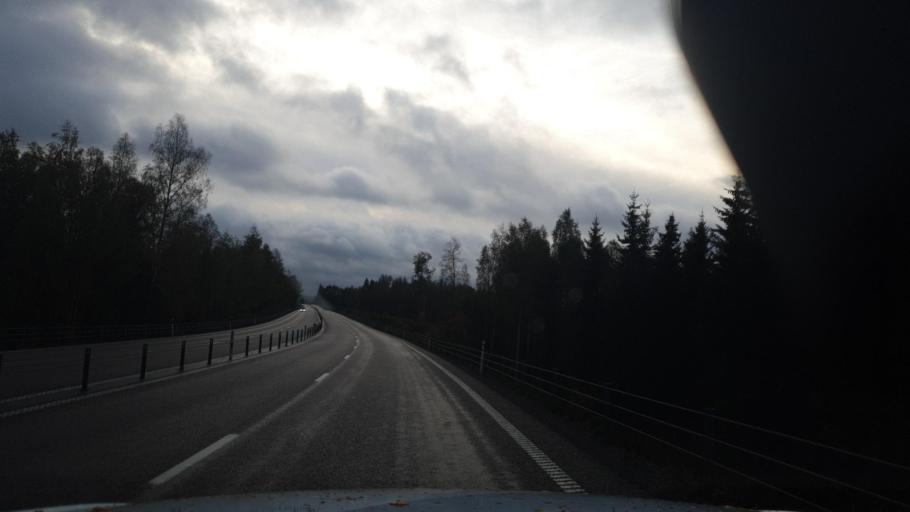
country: SE
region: Vaermland
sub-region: Eda Kommun
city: Amotfors
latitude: 59.7601
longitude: 12.4053
